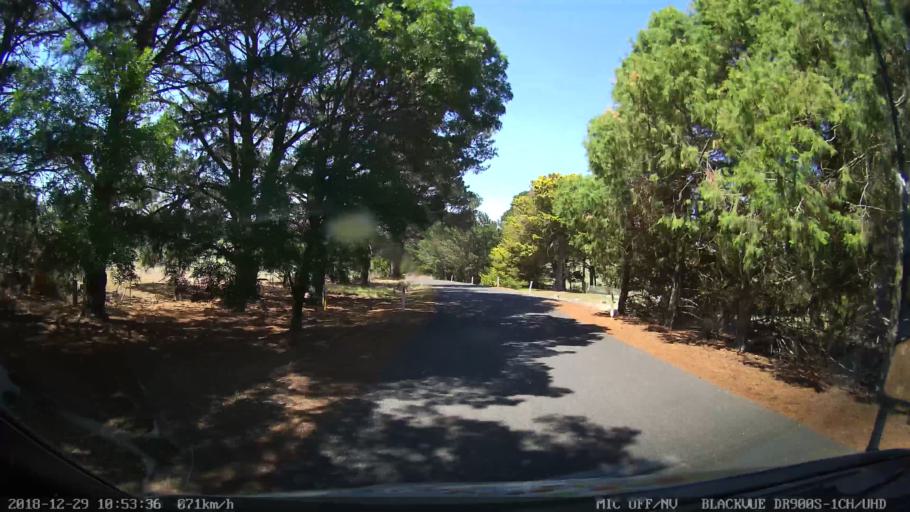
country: AU
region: New South Wales
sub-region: Palerang
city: Bungendore
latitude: -35.1105
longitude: 149.5216
